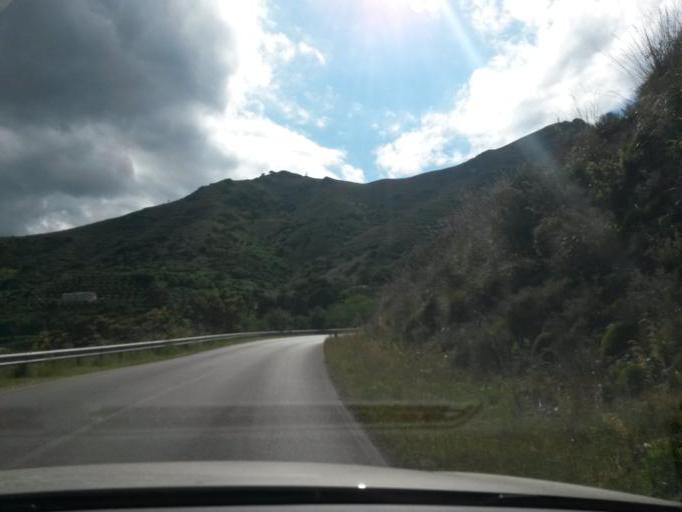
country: IT
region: Tuscany
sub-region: Provincia di Livorno
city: Rio nell'Elba
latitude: 42.8002
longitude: 10.4037
